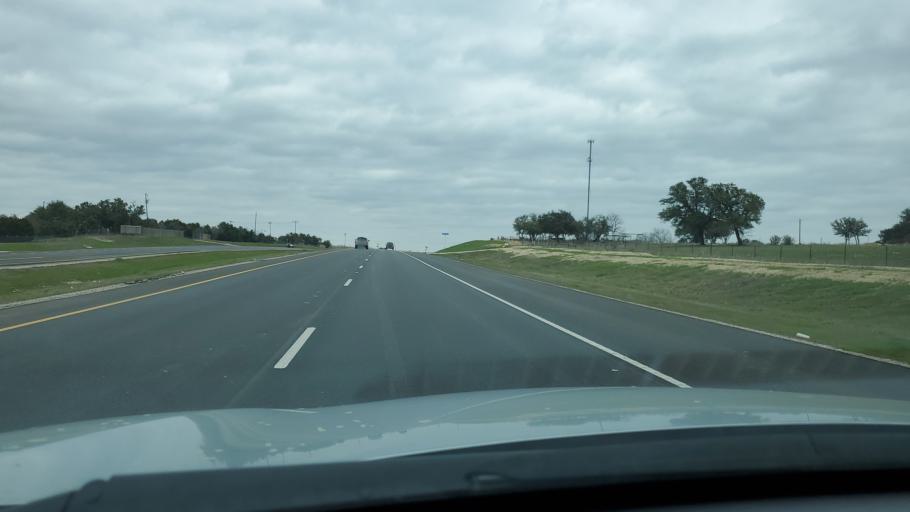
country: US
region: Texas
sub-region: Williamson County
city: Florence
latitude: 30.9303
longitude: -97.7922
